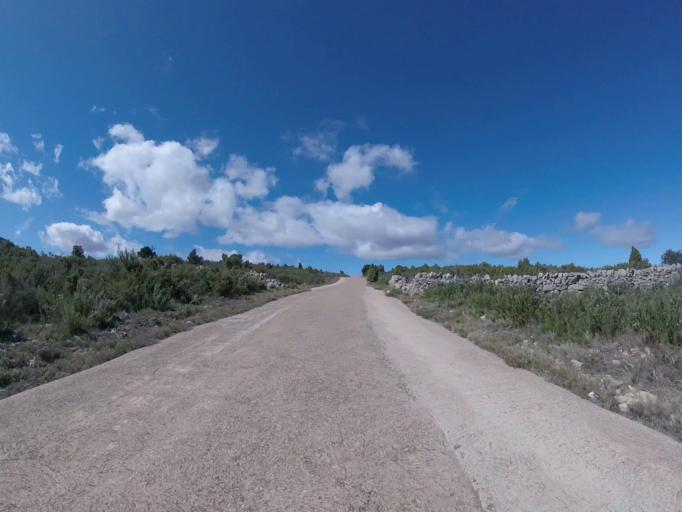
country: ES
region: Valencia
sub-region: Provincia de Castello
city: Culla
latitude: 40.3139
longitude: -0.0959
